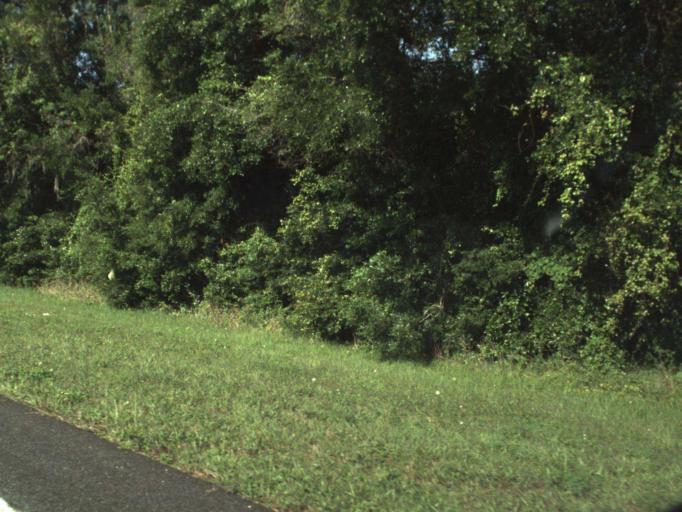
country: US
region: Florida
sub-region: Marion County
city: Citra
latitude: 29.3650
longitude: -82.1374
